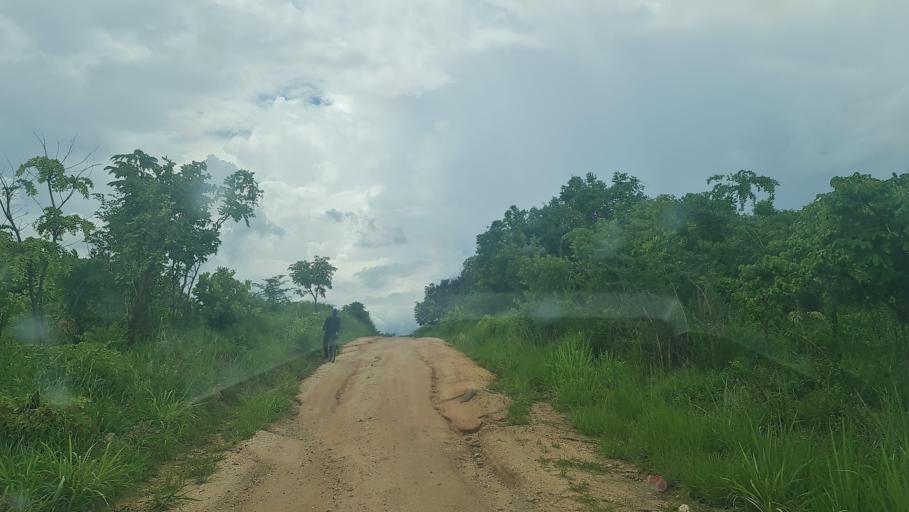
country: MW
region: Southern Region
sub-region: Nsanje District
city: Nsanje
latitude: -17.5906
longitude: 35.6735
